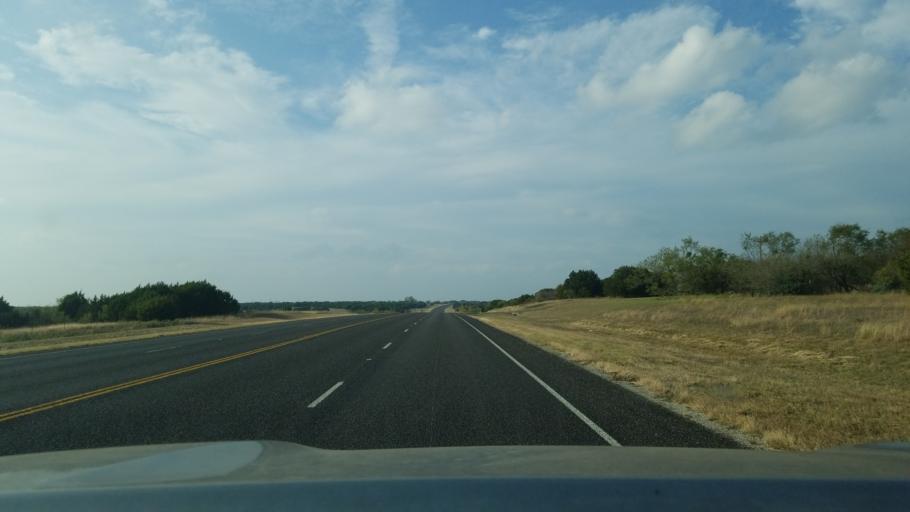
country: US
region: Texas
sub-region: Mills County
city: Goldthwaite
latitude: 31.2325
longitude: -98.4124
